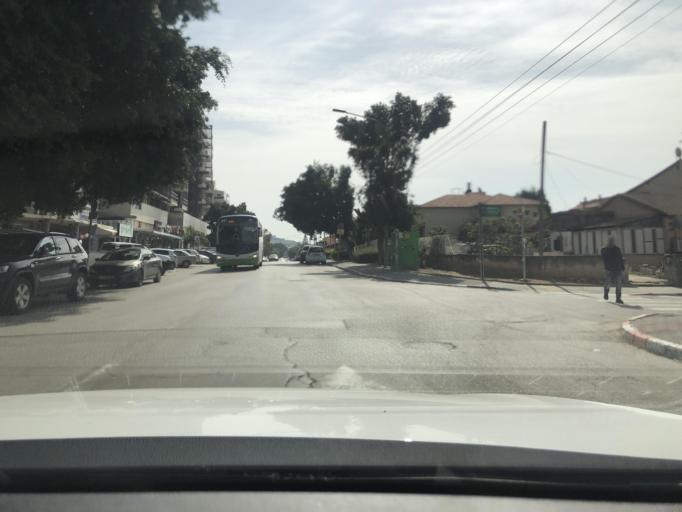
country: IL
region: Central District
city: Rosh Ha'Ayin
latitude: 32.0949
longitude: 34.9449
